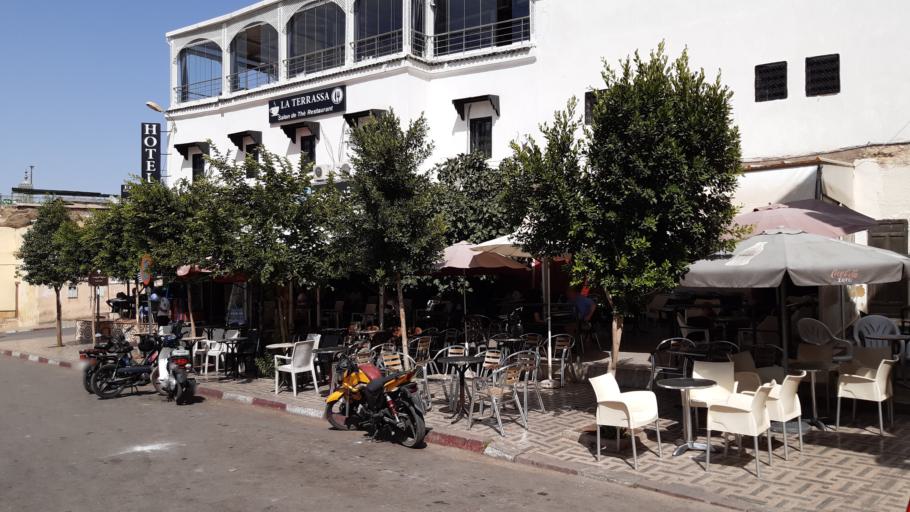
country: MA
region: Fes-Boulemane
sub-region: Fes
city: Fes
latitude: 34.0613
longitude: -4.9844
